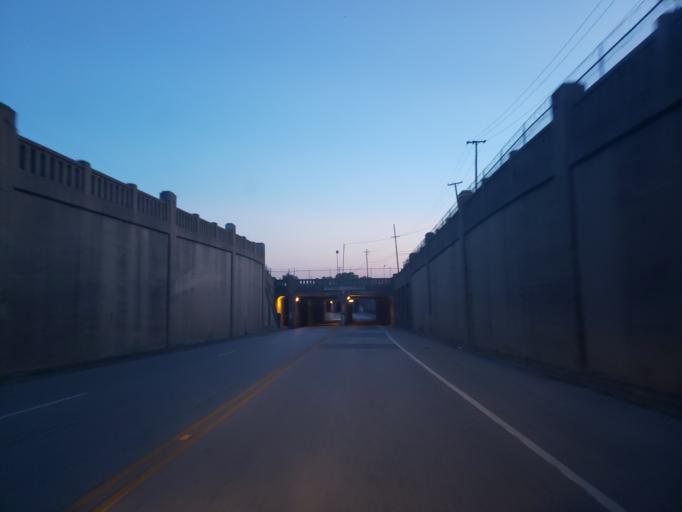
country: US
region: Texas
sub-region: Dallas County
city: Dallas
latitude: 32.7638
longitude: -96.7909
